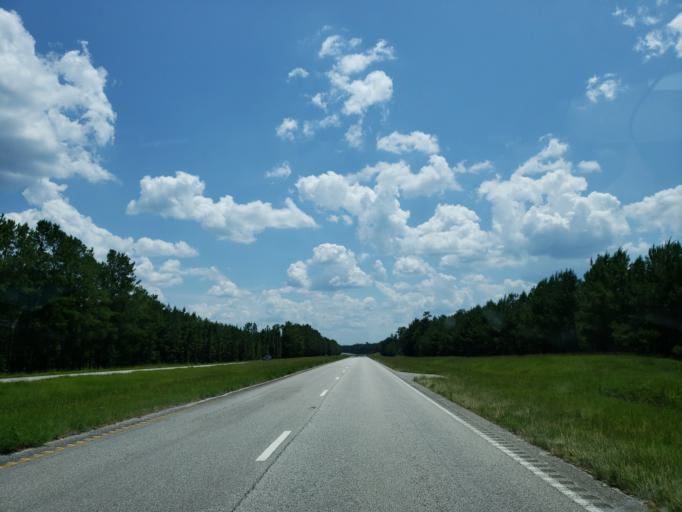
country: US
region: Mississippi
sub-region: Greene County
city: Leakesville
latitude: 31.3364
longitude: -88.5048
